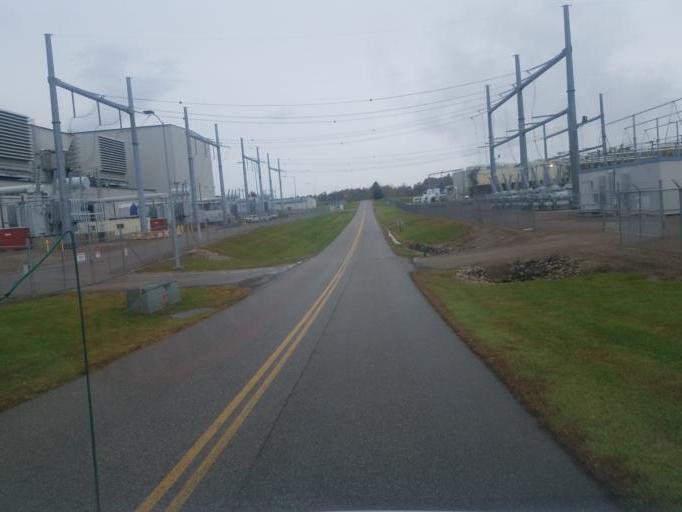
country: US
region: Ohio
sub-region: Washington County
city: Beverly
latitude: 39.5323
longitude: -81.7161
